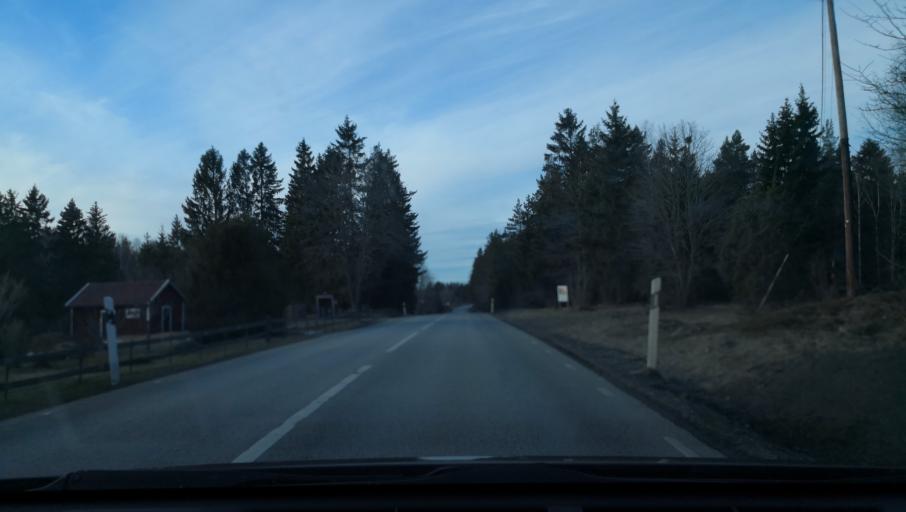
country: SE
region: Uppsala
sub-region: Osthammars Kommun
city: Gimo
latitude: 60.3401
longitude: 18.2153
